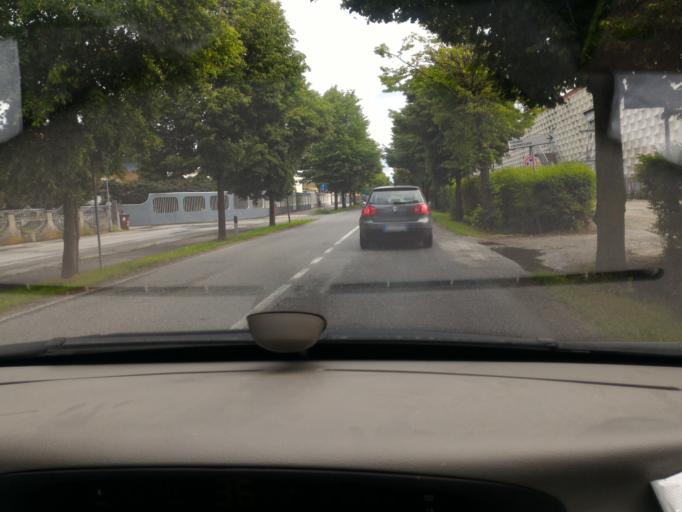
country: IT
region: Piedmont
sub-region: Provincia di Cuneo
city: Genola
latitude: 44.5949
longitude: 7.6593
